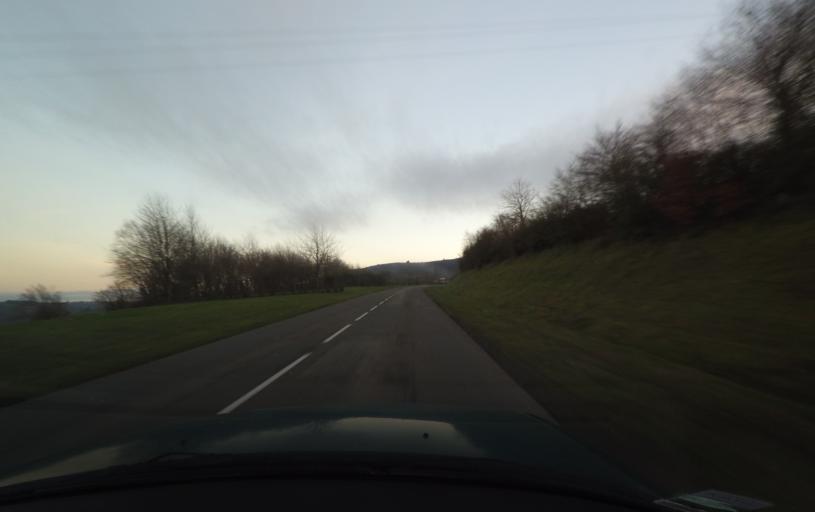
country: FR
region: Pays de la Loire
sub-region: Departement de la Mayenne
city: Bais
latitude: 48.2068
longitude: -0.3671
